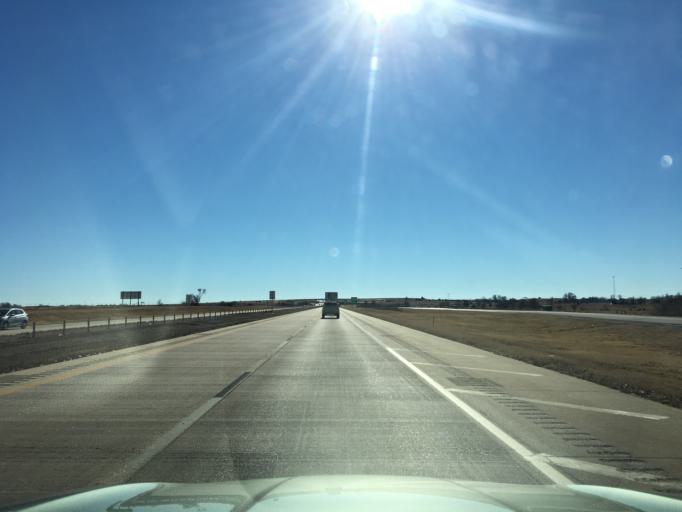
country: US
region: Oklahoma
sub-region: Noble County
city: Perry
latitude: 36.4150
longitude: -97.3272
